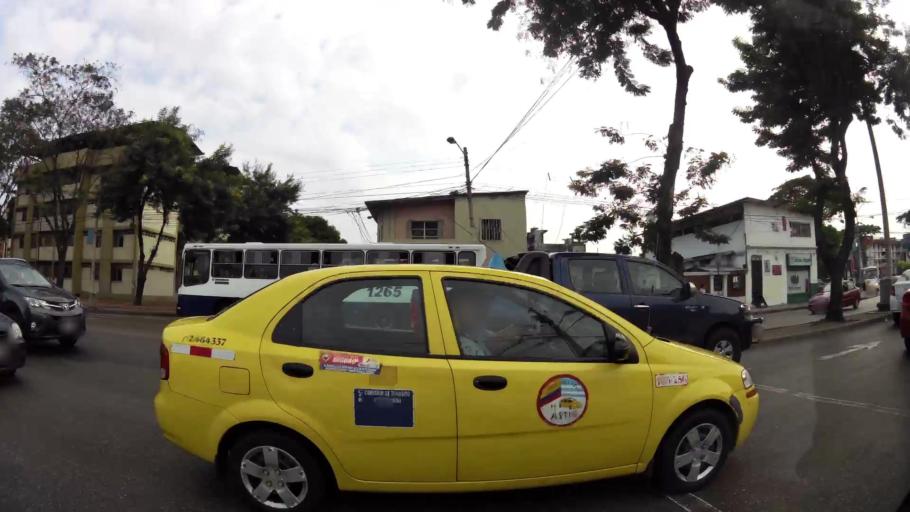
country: EC
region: Guayas
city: Guayaquil
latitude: -2.2391
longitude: -79.8922
